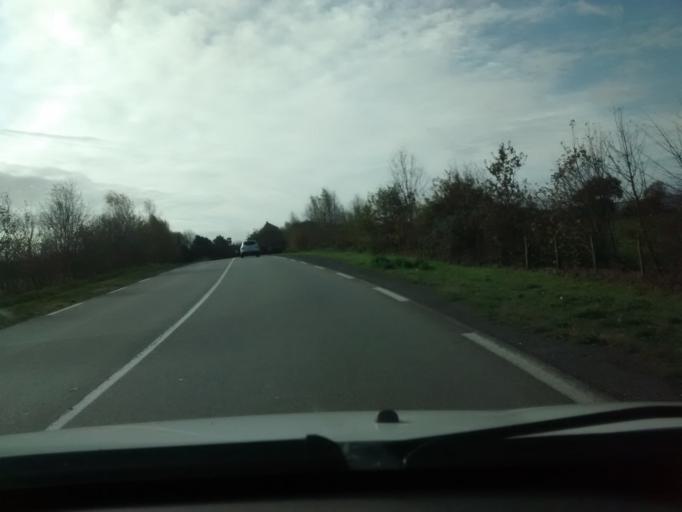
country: FR
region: Brittany
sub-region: Departement d'Ille-et-Vilaine
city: Cesson-Sevigne
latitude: 48.1184
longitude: -1.5746
